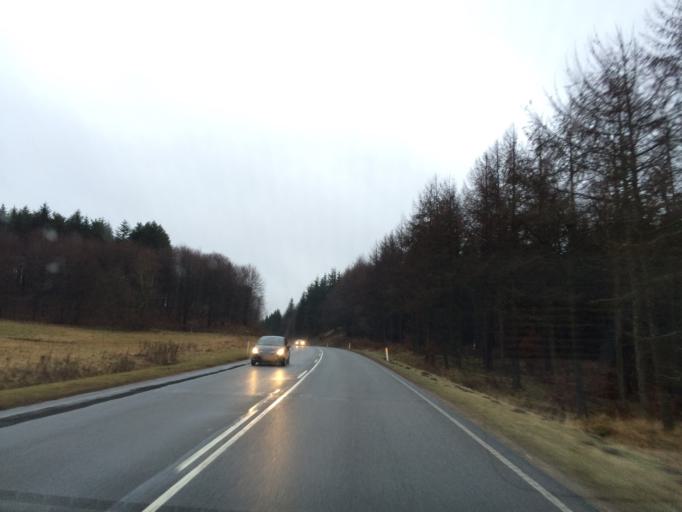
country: DK
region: North Denmark
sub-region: Mariagerfjord Kommune
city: Arden
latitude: 56.8037
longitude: 9.8171
